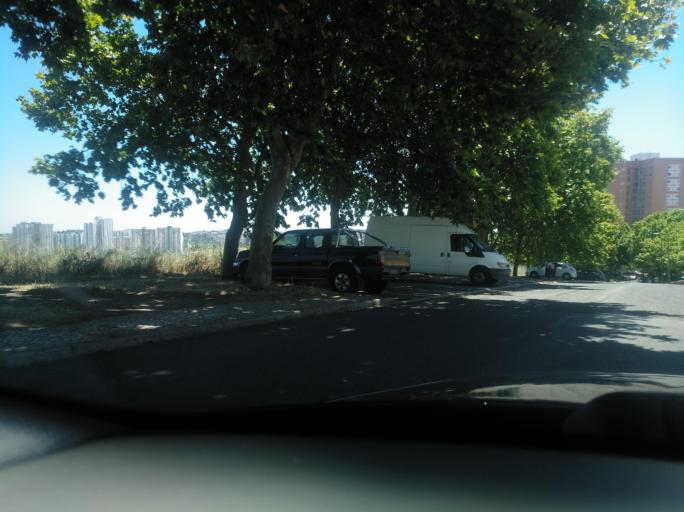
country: PT
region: Lisbon
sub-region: Odivelas
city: Povoa de Santo Adriao
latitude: 38.8113
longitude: -9.1774
